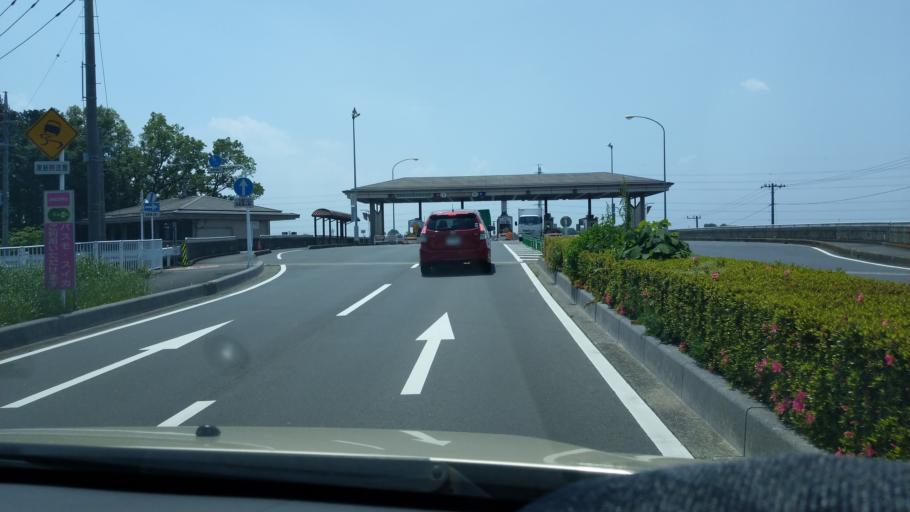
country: JP
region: Saitama
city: Saitama
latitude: 35.8874
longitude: 139.7056
